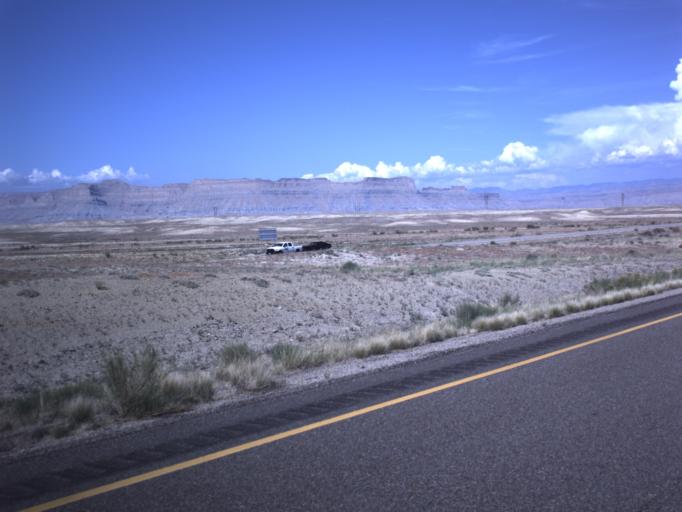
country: US
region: Utah
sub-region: Carbon County
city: East Carbon City
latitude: 38.9609
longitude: -110.2882
